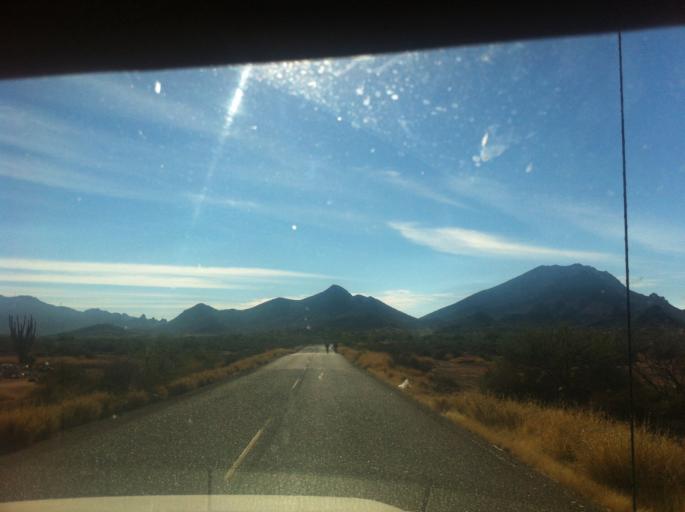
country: MX
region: Sonora
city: Heroica Guaymas
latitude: 27.9762
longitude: -110.9692
